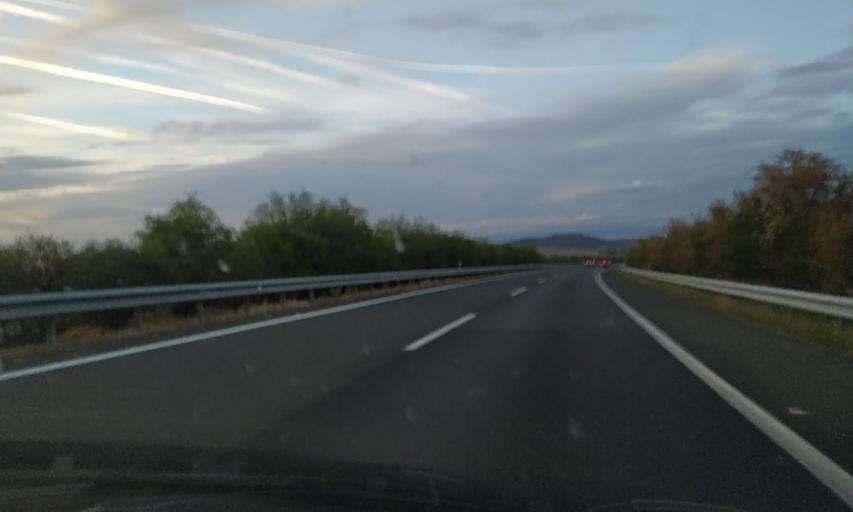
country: ES
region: Extremadura
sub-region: Provincia de Caceres
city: Aldea del Cano
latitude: 39.3487
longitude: -6.3426
